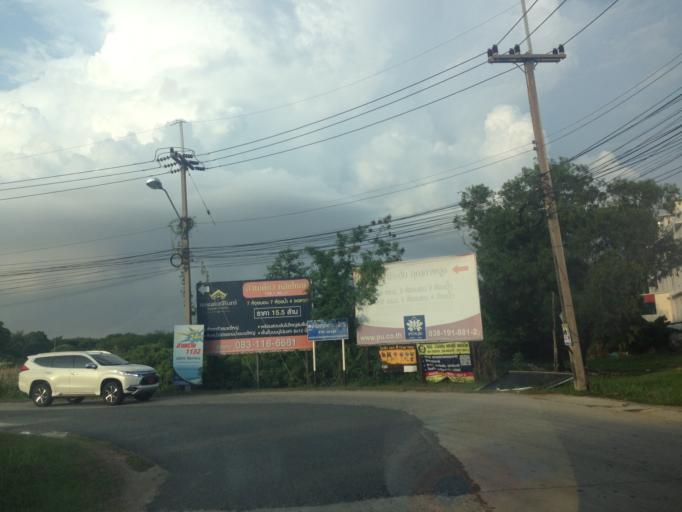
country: TH
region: Chon Buri
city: Chon Buri
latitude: 13.2977
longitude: 100.9217
